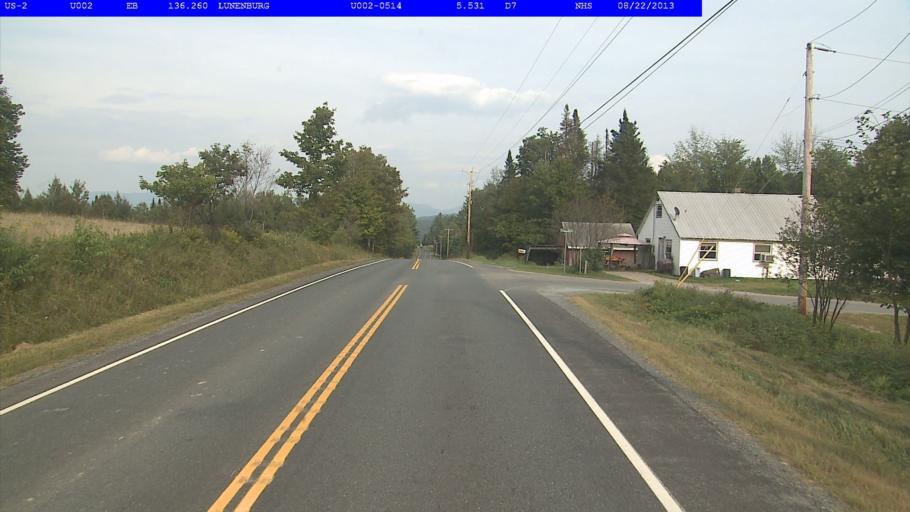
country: US
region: New Hampshire
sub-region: Coos County
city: Lancaster
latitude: 44.4642
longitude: -71.6656
